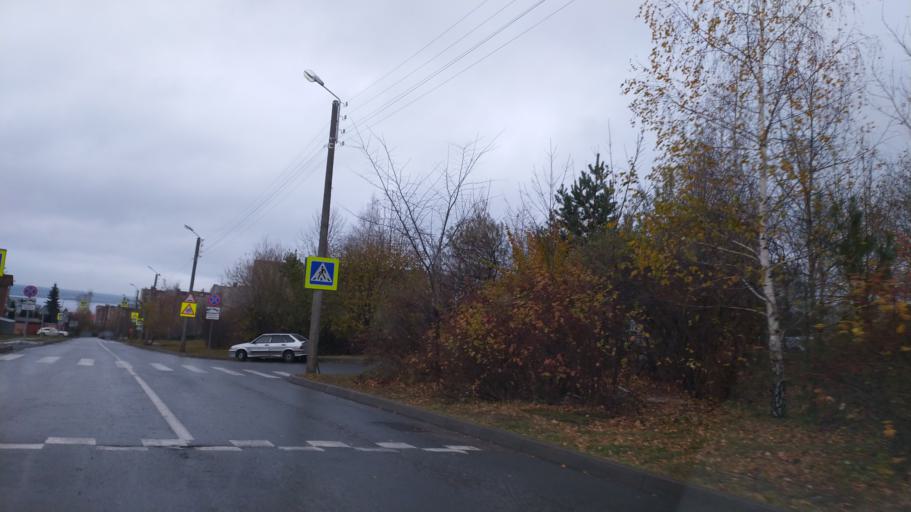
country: RU
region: Chuvashia
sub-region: Cheboksarskiy Rayon
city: Cheboksary
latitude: 56.1453
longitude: 47.1617
